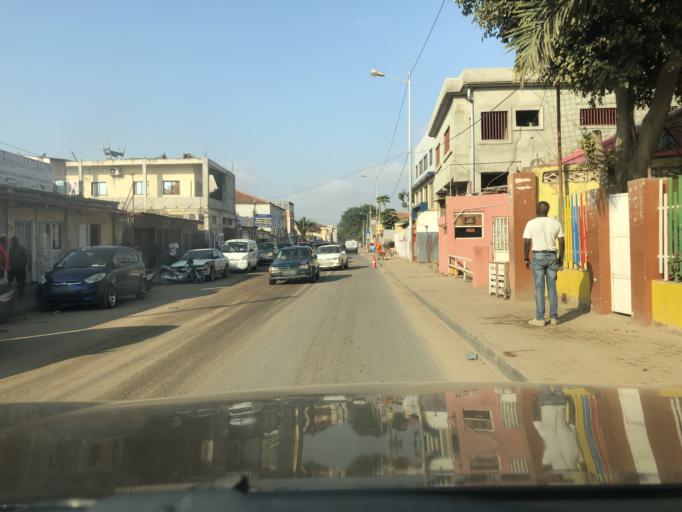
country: AO
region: Luanda
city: Luanda
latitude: -8.8416
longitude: 13.2621
